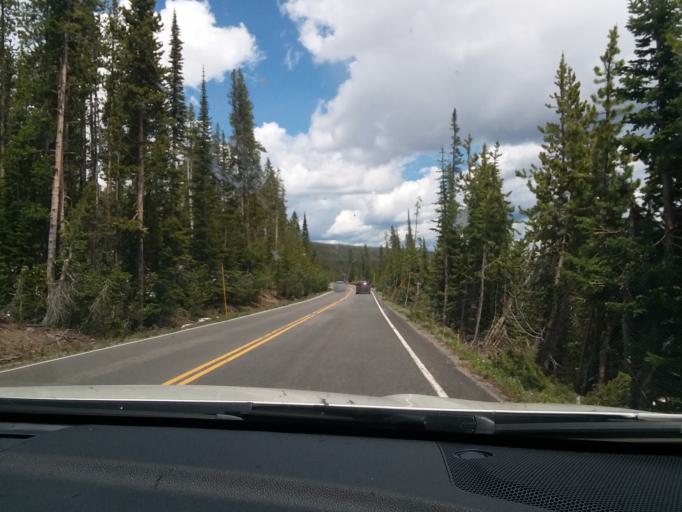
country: US
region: Montana
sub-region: Gallatin County
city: West Yellowstone
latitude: 44.2022
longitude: -110.6600
